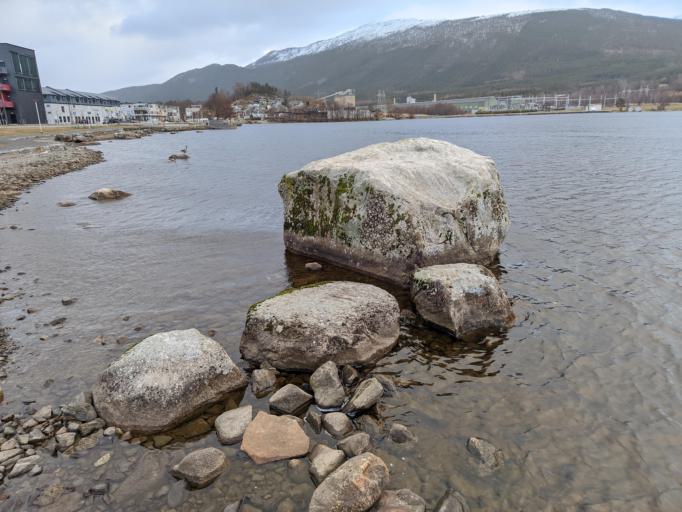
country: NO
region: Rogaland
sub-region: Vindafjord
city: Olen
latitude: 59.8594
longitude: 5.7562
